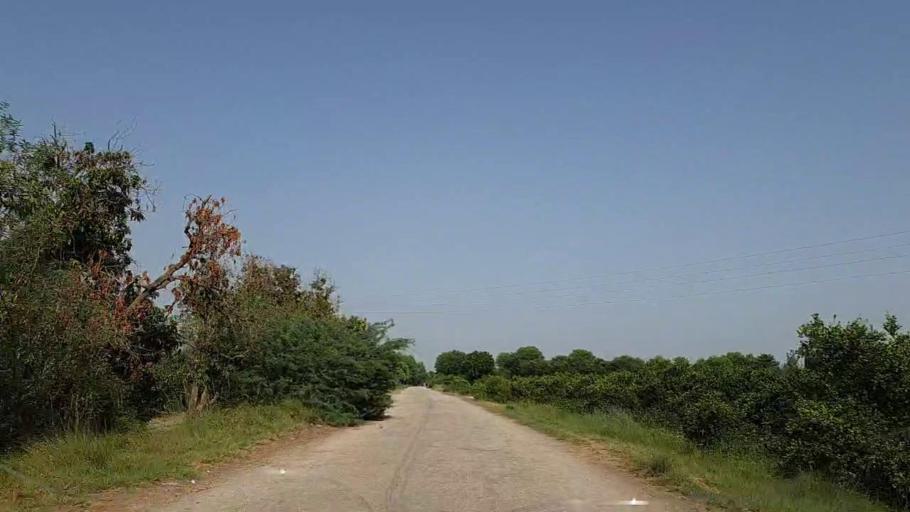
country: PK
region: Sindh
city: Kandiaro
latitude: 27.0648
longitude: 68.1893
